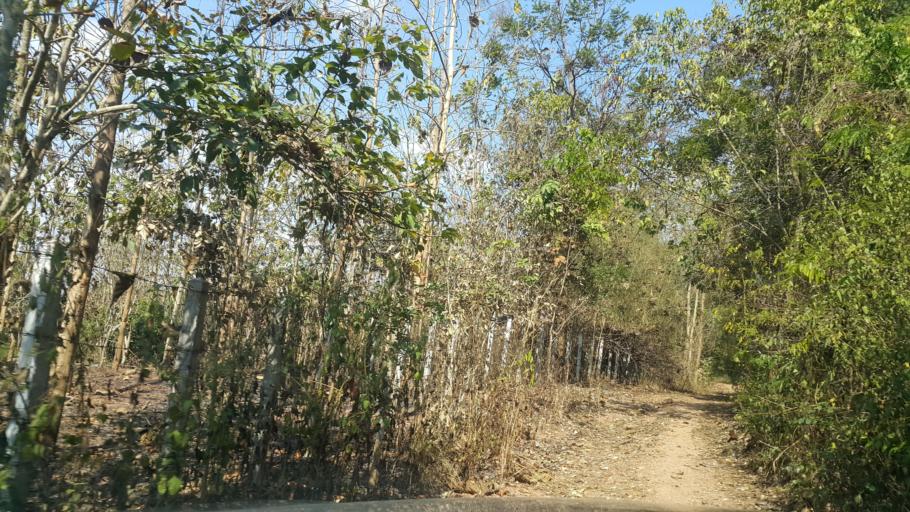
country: TH
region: Sukhothai
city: Thung Saliam
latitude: 17.3543
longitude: 99.5795
